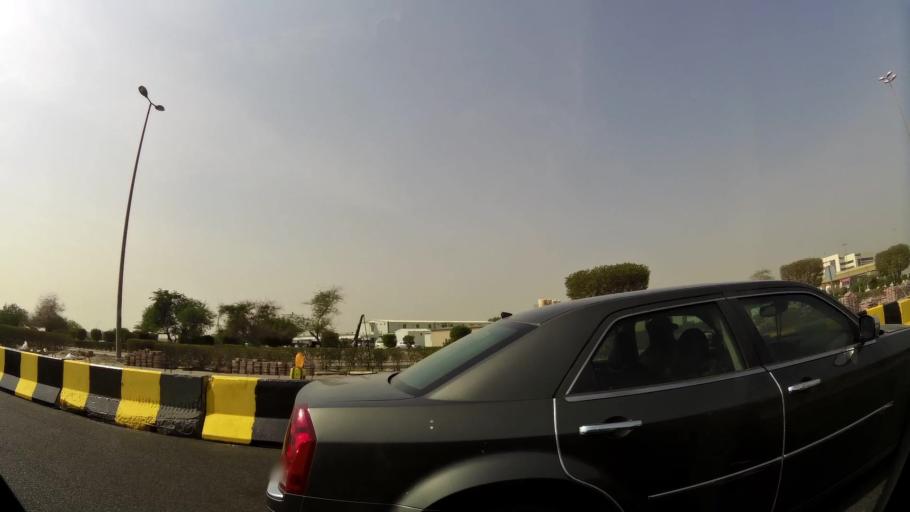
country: KW
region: Al Asimah
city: Ar Rabiyah
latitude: 29.3087
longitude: 47.8656
